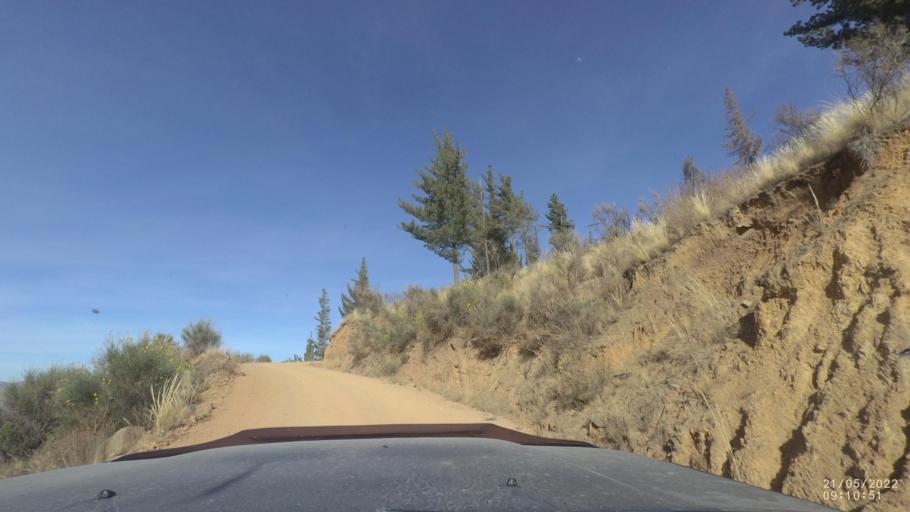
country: BO
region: Cochabamba
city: Cochabamba
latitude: -17.3719
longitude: -66.0223
